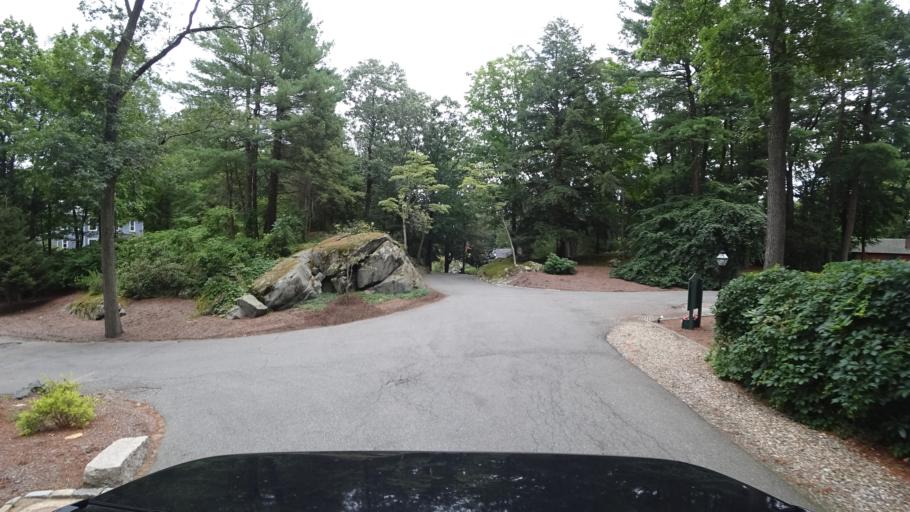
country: US
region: Massachusetts
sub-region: Norfolk County
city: Dedham
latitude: 42.2532
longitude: -71.1923
